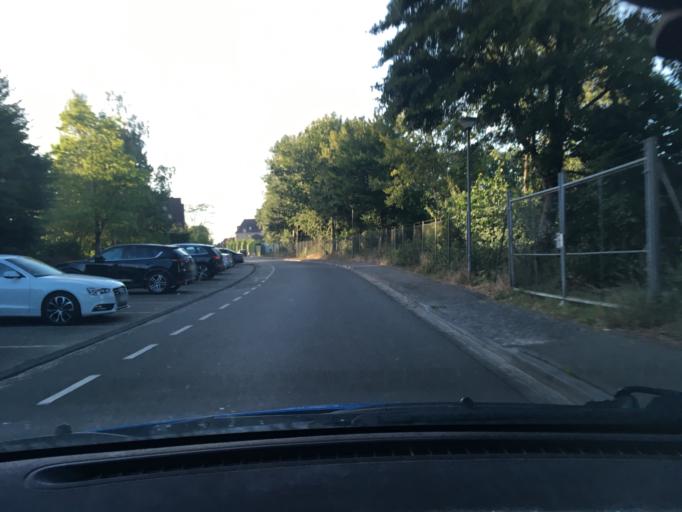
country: DE
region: Lower Saxony
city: Celle
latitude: 52.6288
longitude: 10.0999
